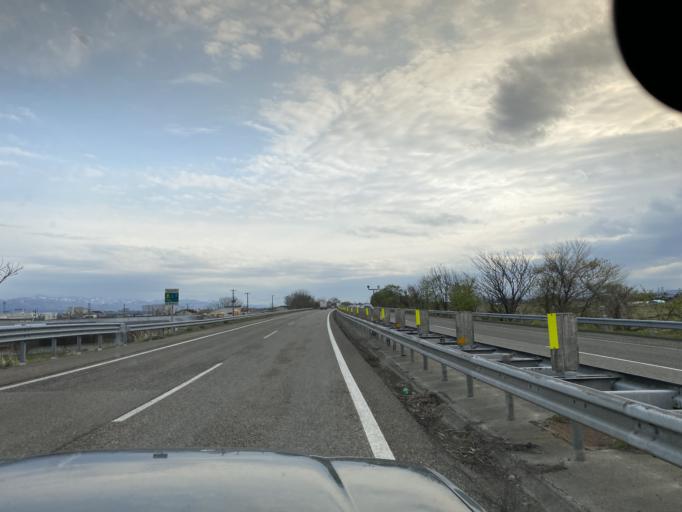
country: JP
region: Niigata
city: Mitsuke
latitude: 37.5705
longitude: 138.8875
